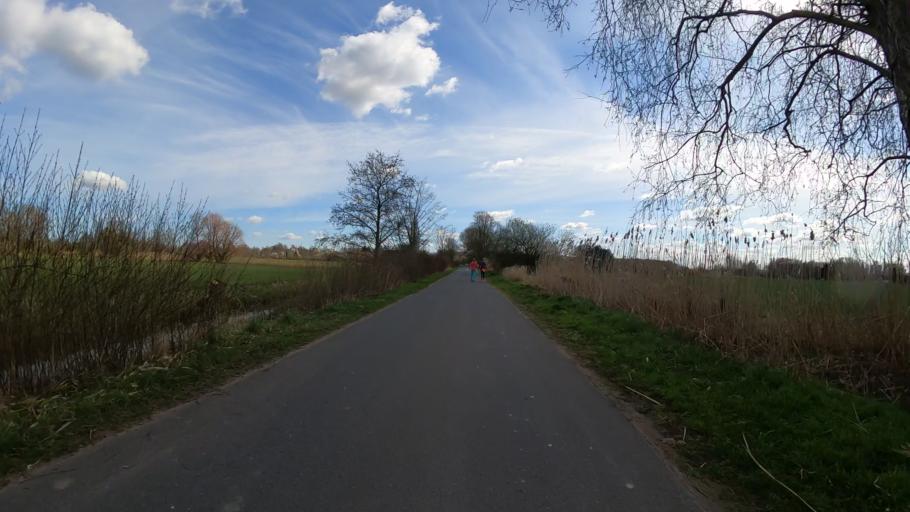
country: DE
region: Lower Saxony
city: Winsen
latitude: 53.4087
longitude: 10.1971
